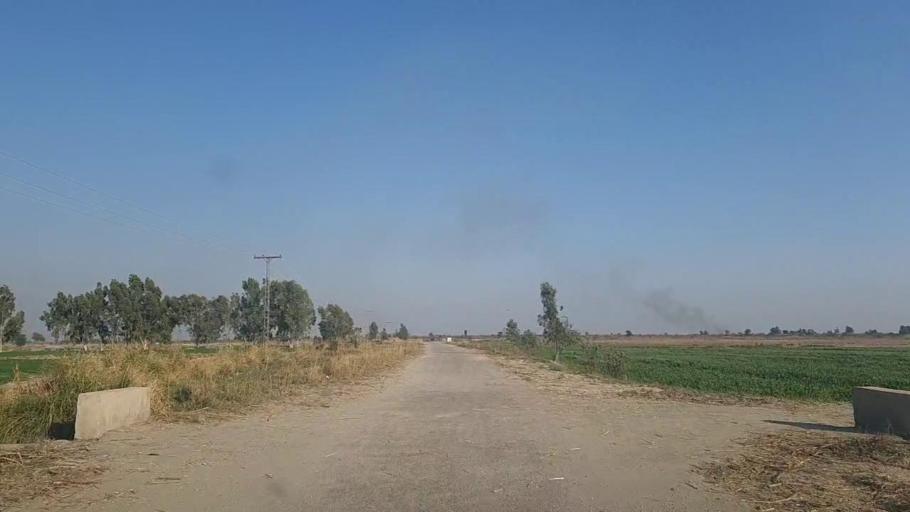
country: PK
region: Sindh
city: Jam Sahib
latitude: 26.3354
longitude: 68.7557
